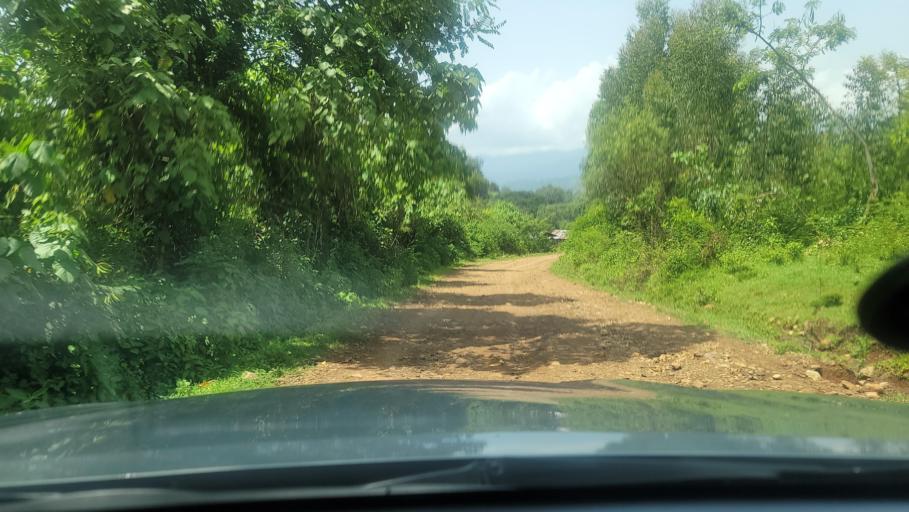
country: ET
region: Oromiya
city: Agaro
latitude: 7.8023
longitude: 36.4169
